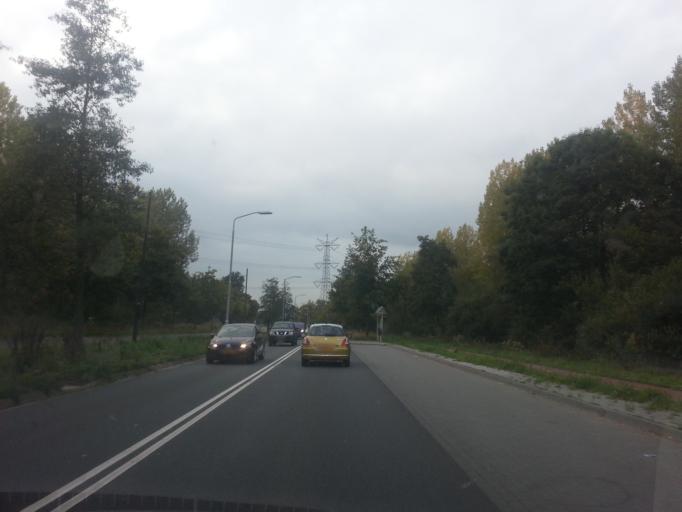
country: NL
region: North Brabant
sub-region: Gemeente Eindhoven
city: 't Hofke
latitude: 51.4676
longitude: 5.5101
